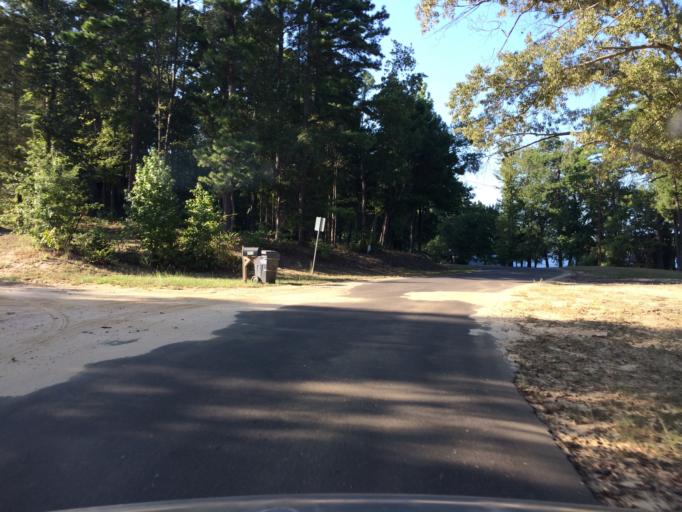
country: US
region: Texas
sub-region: Wood County
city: Hawkins
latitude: 32.6225
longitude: -95.2542
